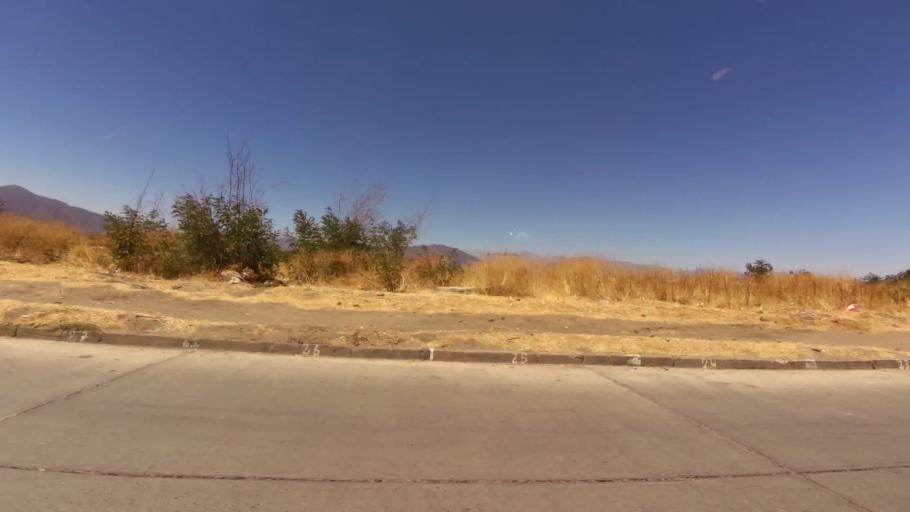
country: CL
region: O'Higgins
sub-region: Provincia de Cachapoal
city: Rancagua
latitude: -34.1590
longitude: -70.7025
